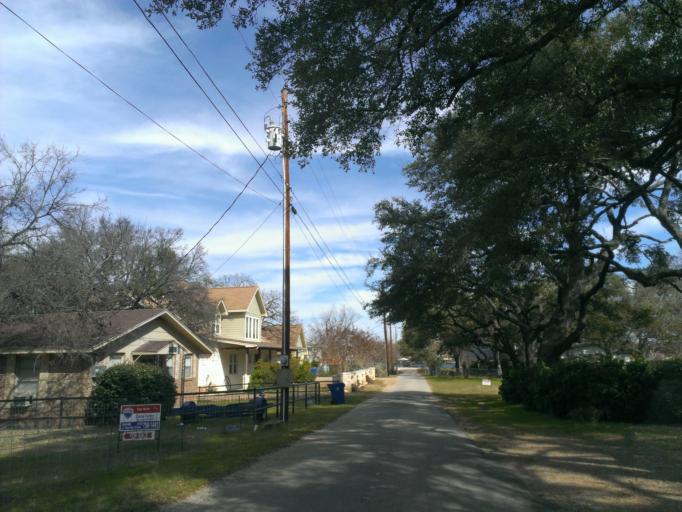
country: US
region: Texas
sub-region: Burnet County
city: Granite Shoals
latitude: 30.5749
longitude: -98.3867
